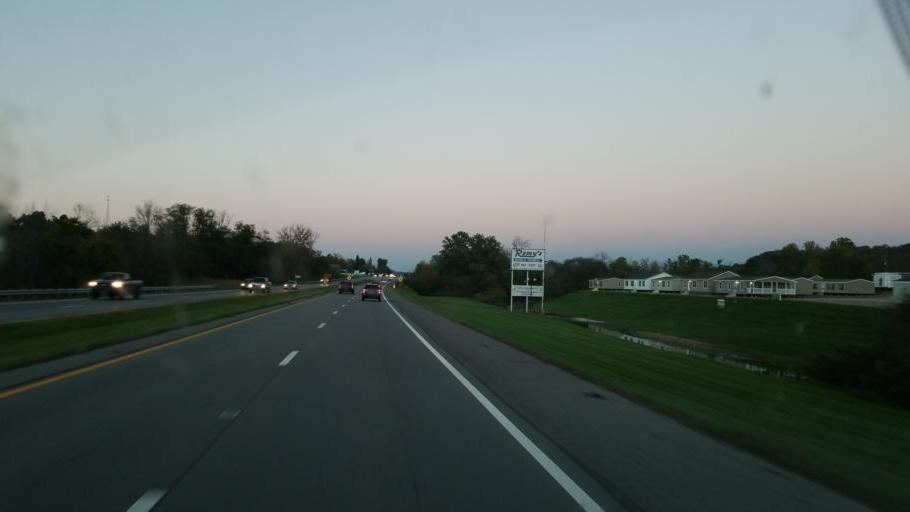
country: US
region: Ohio
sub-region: Ross County
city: Chillicothe
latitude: 39.2788
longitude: -82.9575
